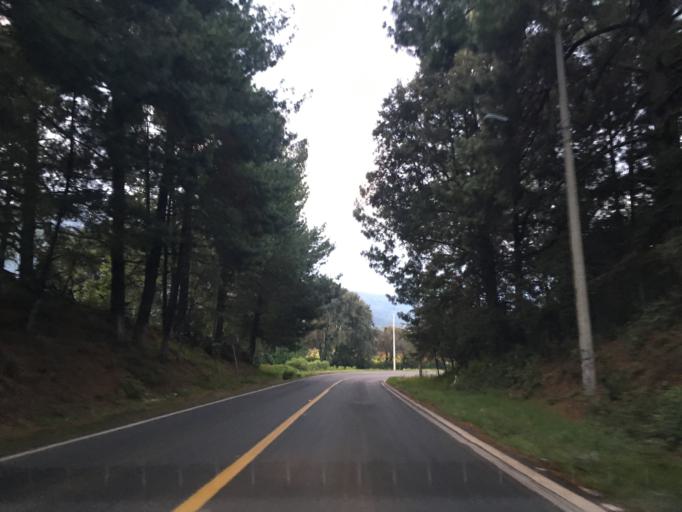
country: MX
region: Michoacan
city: Cheran
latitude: 19.6897
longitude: -101.9630
